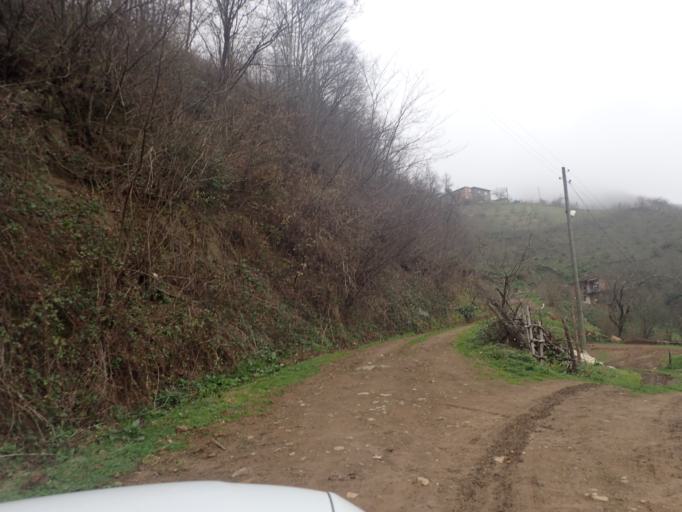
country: TR
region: Ordu
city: Camas
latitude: 40.9006
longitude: 37.5558
